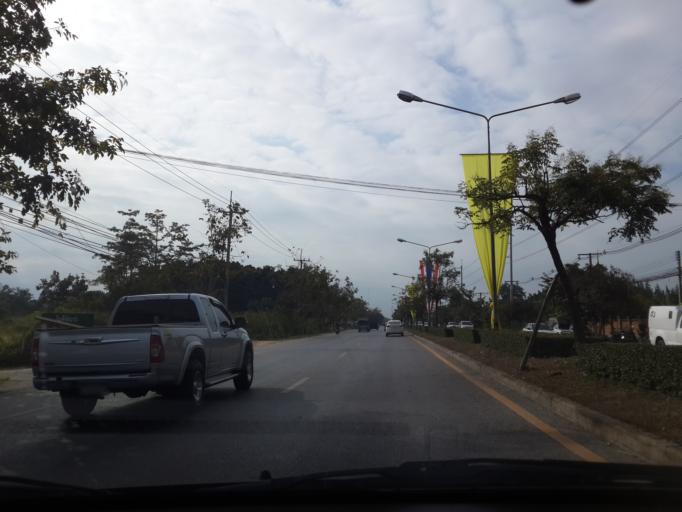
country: TH
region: Chiang Mai
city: San Sai
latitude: 18.8549
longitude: 99.0143
